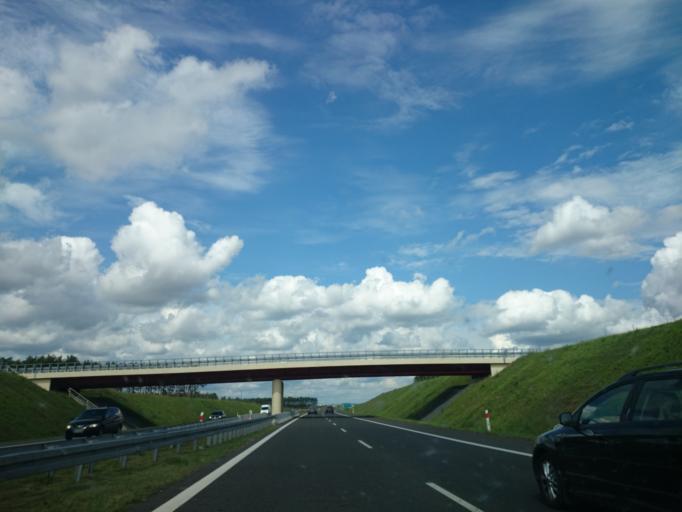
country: PL
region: Lubusz
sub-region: Powiat swiebodzinski
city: Swiebodzin
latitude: 52.3100
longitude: 15.5451
